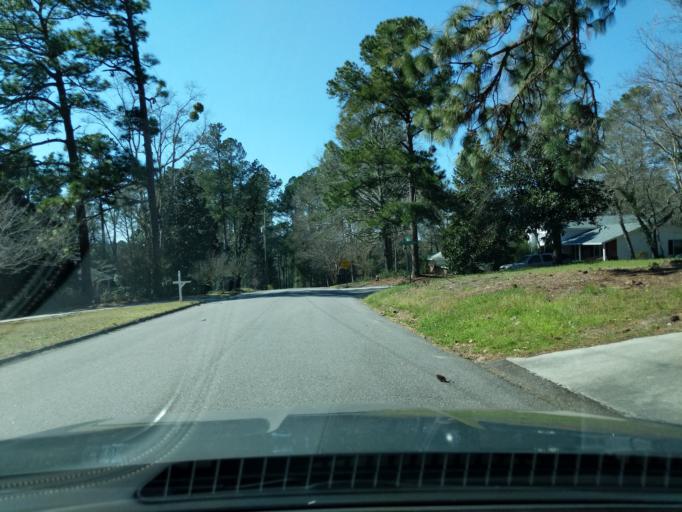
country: US
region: South Carolina
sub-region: Aiken County
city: Aiken
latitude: 33.5329
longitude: -81.7404
